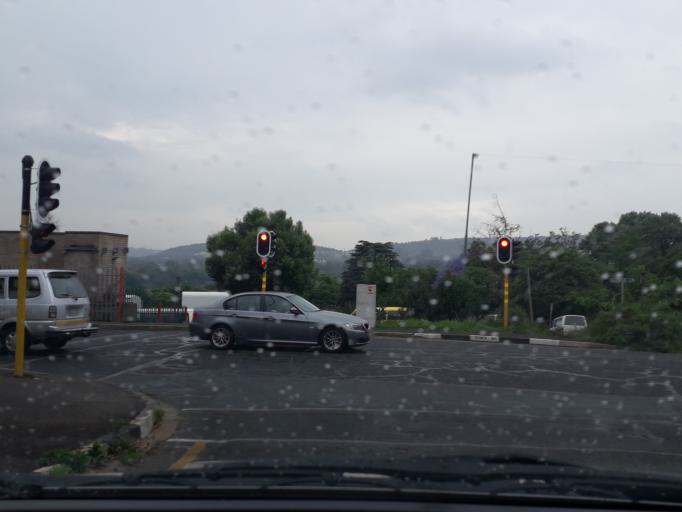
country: ZA
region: Gauteng
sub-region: City of Johannesburg Metropolitan Municipality
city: Modderfontein
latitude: -26.1447
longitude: 28.1073
